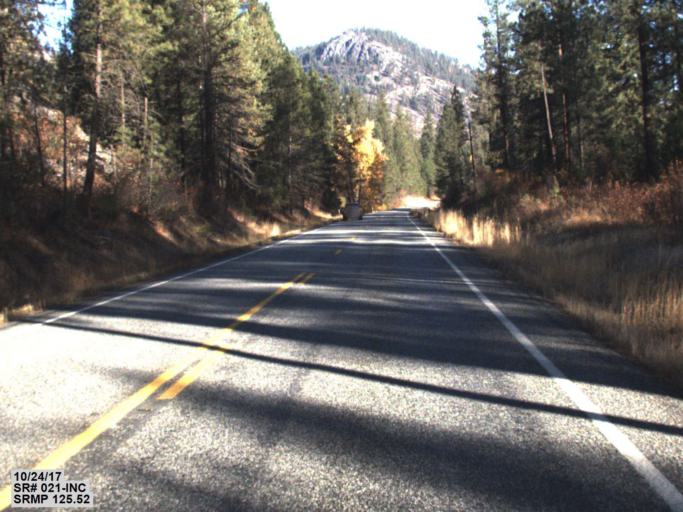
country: US
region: Washington
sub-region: Okanogan County
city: Coulee Dam
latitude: 48.1985
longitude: -118.7138
